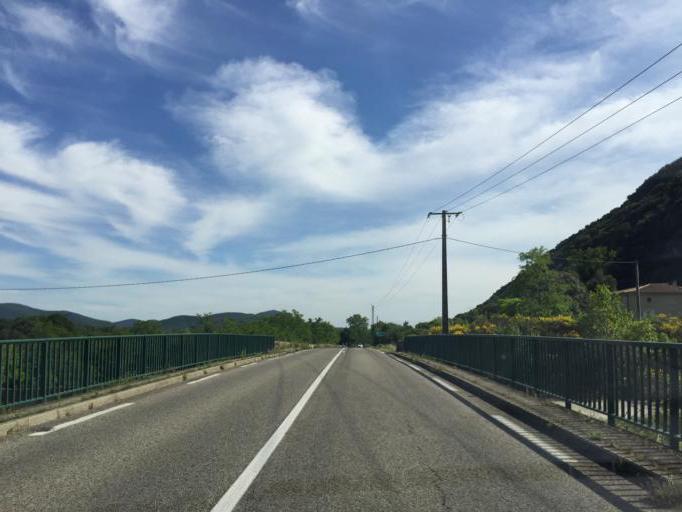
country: FR
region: Rhone-Alpes
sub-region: Departement de l'Ardeche
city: Cruas
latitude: 44.6801
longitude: 4.7715
